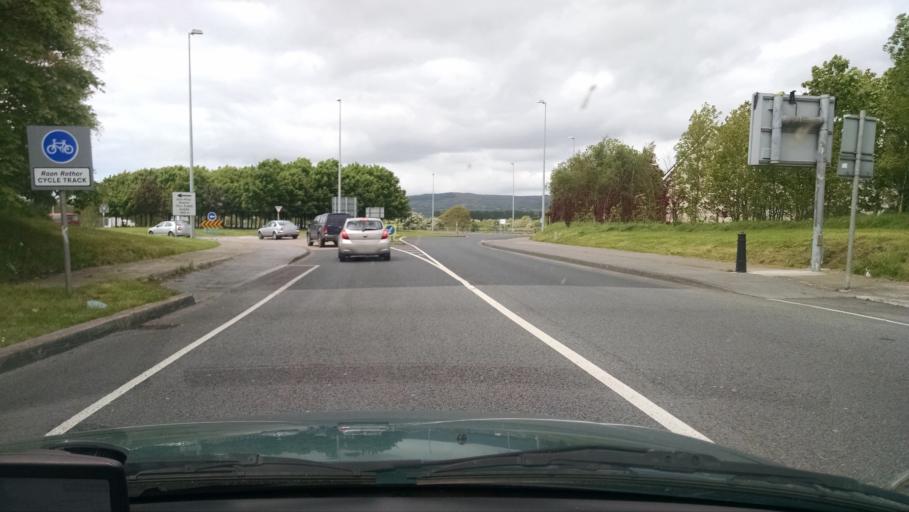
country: IE
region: Munster
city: Moyross
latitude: 52.6645
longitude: -8.6687
